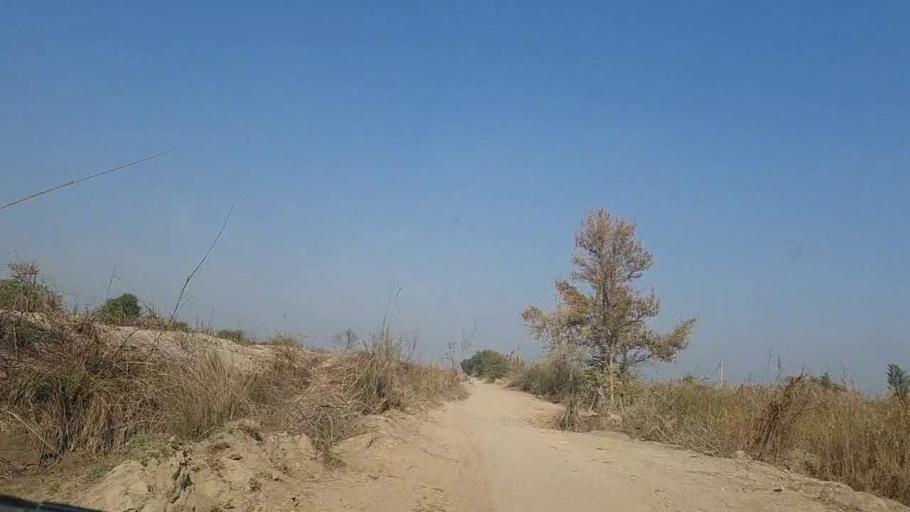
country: PK
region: Sindh
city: Sakrand
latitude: 26.0749
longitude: 68.3564
